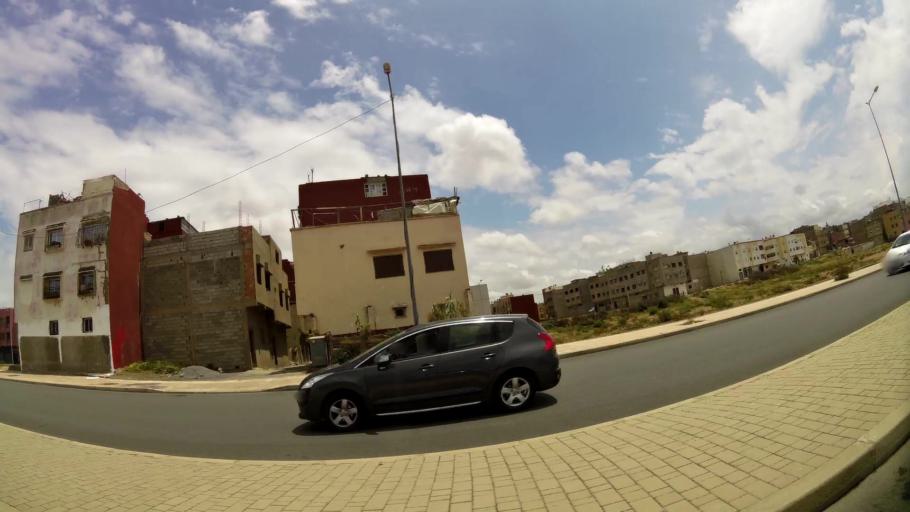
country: MA
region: Rabat-Sale-Zemmour-Zaer
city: Sale
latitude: 34.0632
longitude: -6.8097
